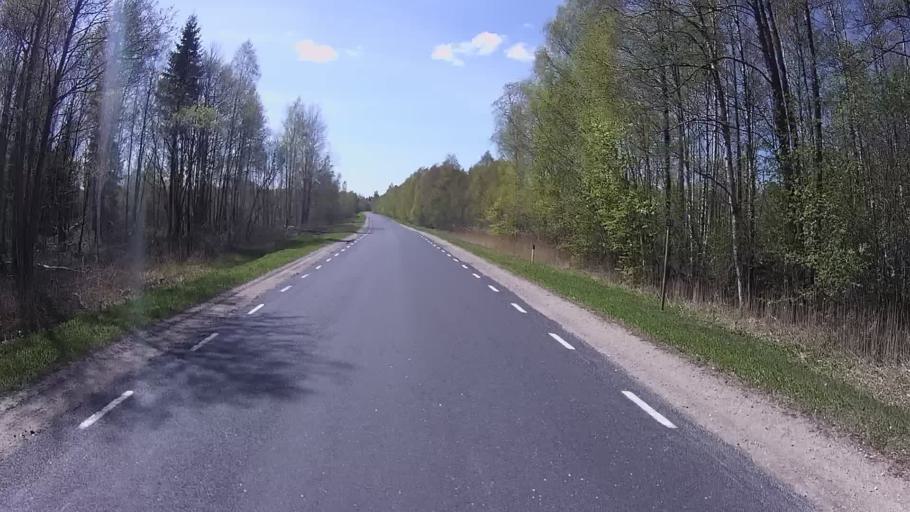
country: EE
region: Laeaene
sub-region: Ridala Parish
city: Uuemoisa
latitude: 59.0246
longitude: 23.8066
